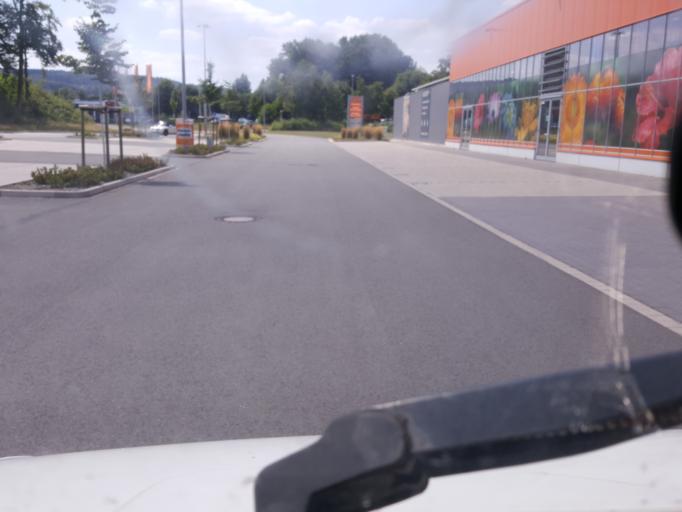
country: DE
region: North Rhine-Westphalia
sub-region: Regierungsbezirk Detmold
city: Minden
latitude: 52.2634
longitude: 8.9003
